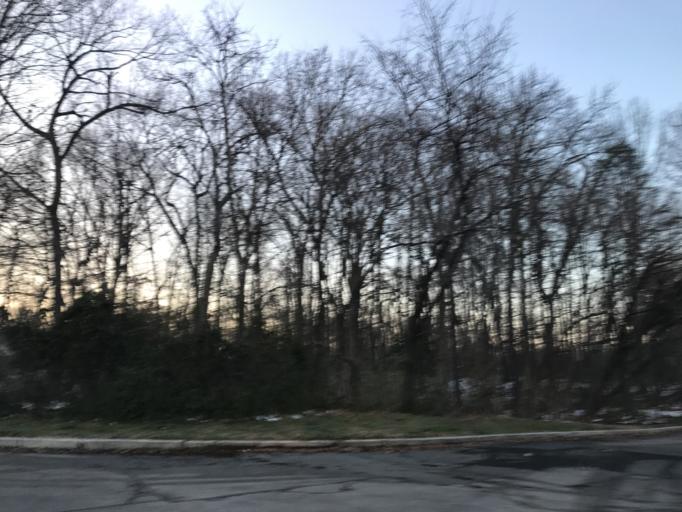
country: US
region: Maryland
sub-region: Baltimore County
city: Middle River
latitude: 39.3146
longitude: -76.4446
